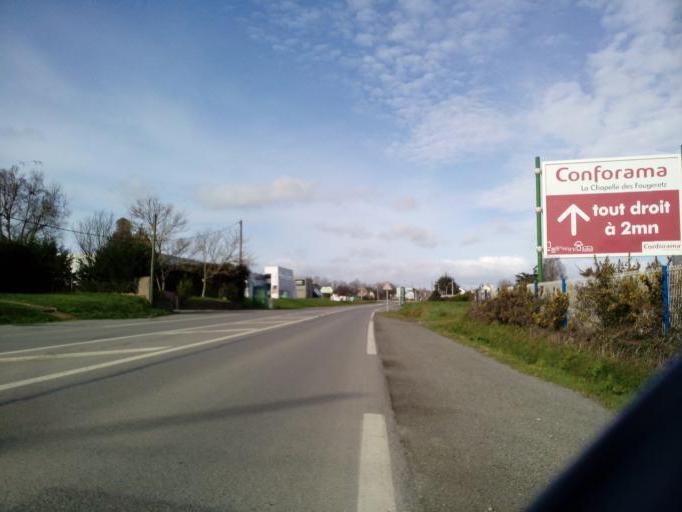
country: FR
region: Brittany
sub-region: Departement d'Ille-et-Vilaine
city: La Chapelle-des-Fougeretz
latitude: 48.1721
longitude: -1.7202
